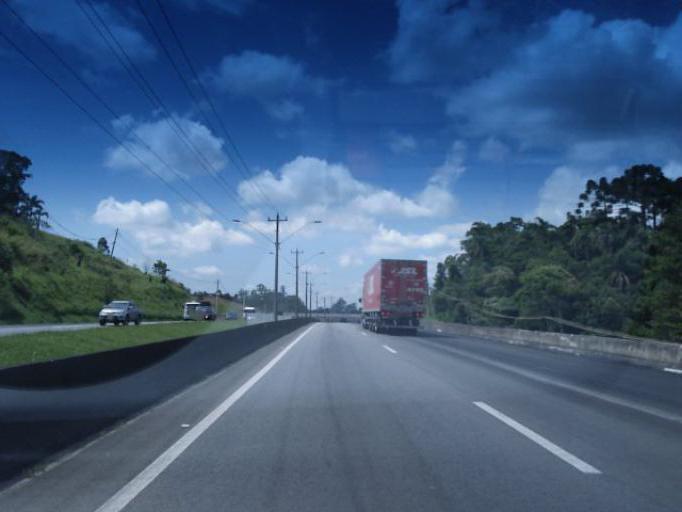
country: BR
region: Sao Paulo
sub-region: Itapecerica Da Serra
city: Itapecerica da Serra
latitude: -23.7317
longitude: -46.8948
